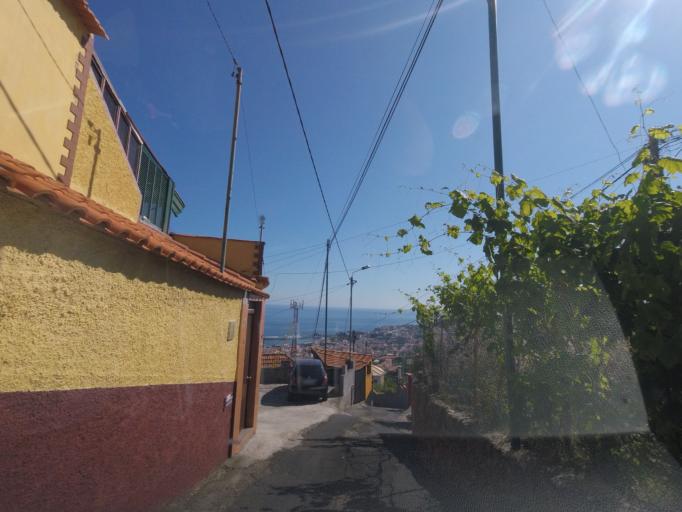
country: PT
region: Madeira
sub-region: Funchal
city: Nossa Senhora do Monte
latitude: 32.6638
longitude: -16.8999
